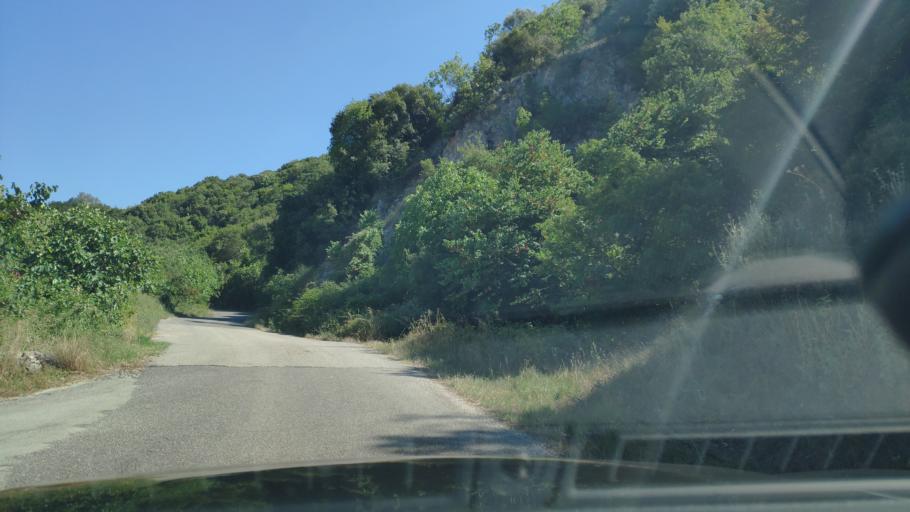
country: GR
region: West Greece
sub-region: Nomos Aitolias kai Akarnanias
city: Katouna
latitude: 38.8243
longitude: 21.1000
